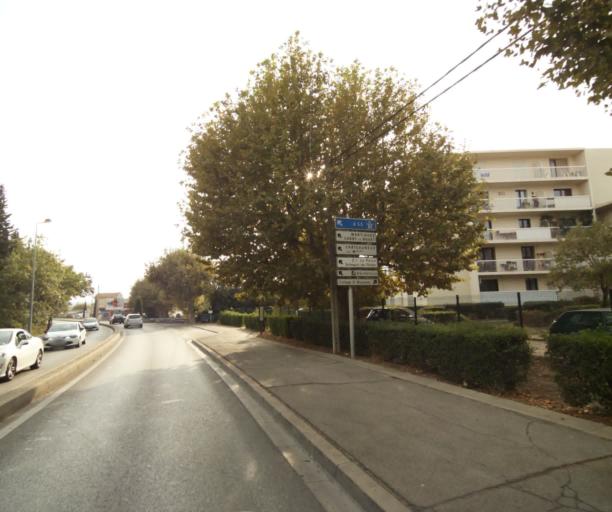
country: FR
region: Provence-Alpes-Cote d'Azur
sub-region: Departement des Bouches-du-Rhone
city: Marignane
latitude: 43.4106
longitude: 5.2098
